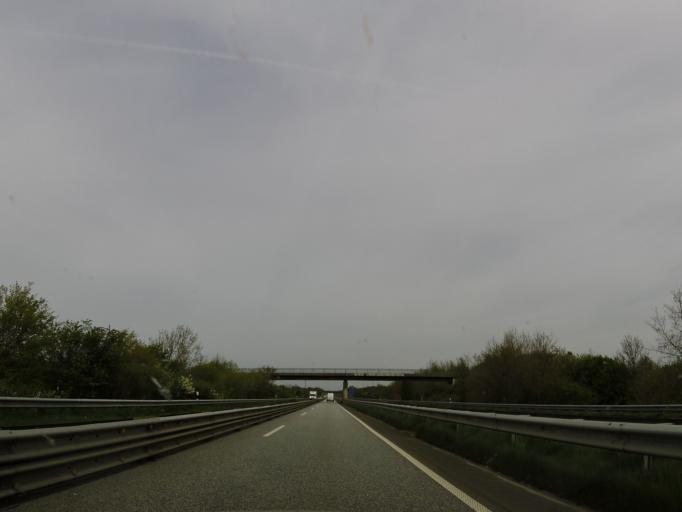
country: DE
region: Schleswig-Holstein
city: Tensbuttel-Rost
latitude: 54.1092
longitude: 9.2625
